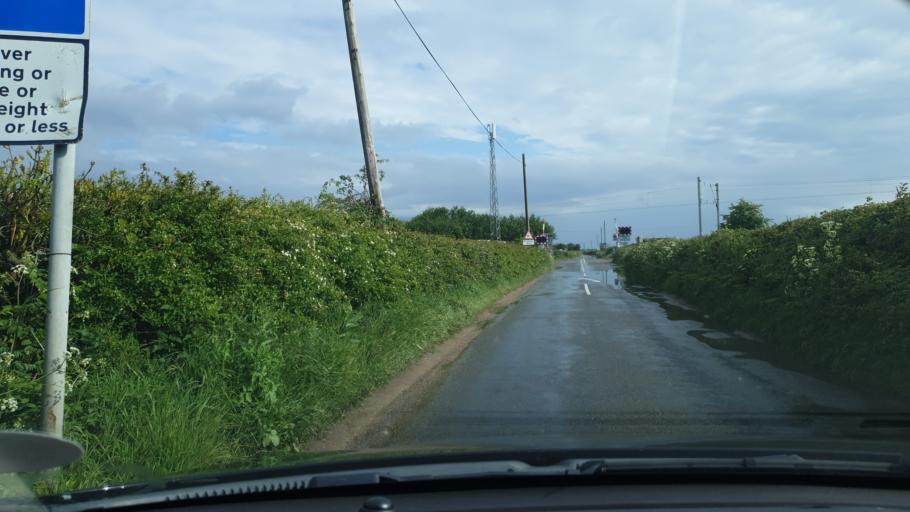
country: GB
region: England
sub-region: Essex
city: Great Bentley
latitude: 51.8500
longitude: 1.0448
